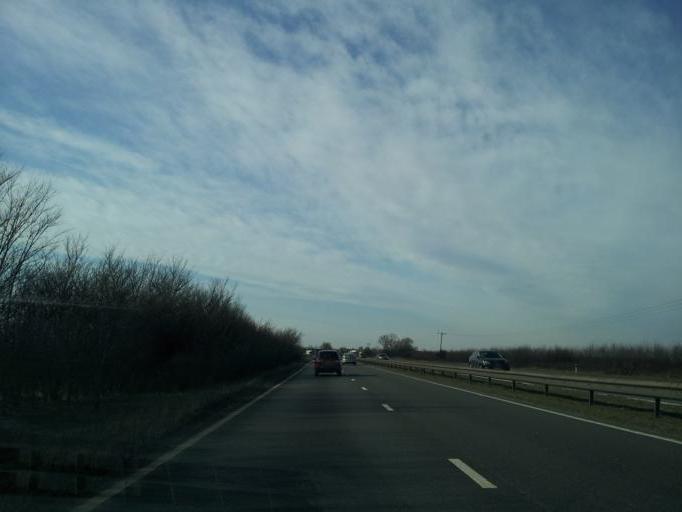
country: GB
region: England
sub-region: Lincolnshire
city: Great Gonerby
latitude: 52.9665
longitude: -0.7008
